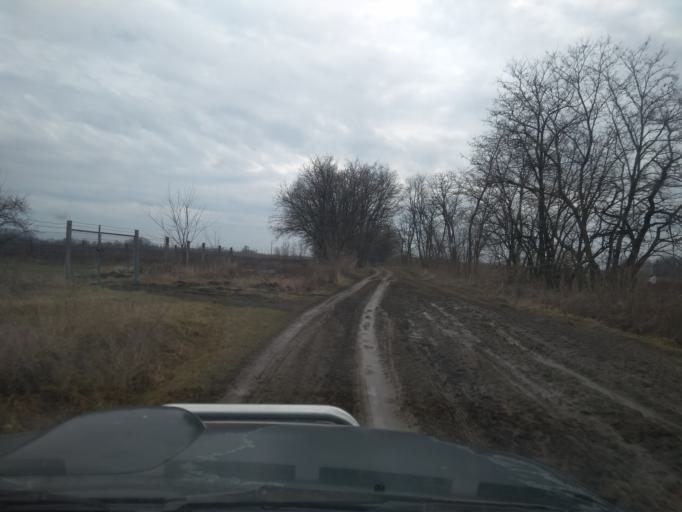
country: HU
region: Szabolcs-Szatmar-Bereg
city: Nyirtelek
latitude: 47.9681
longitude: 21.6524
